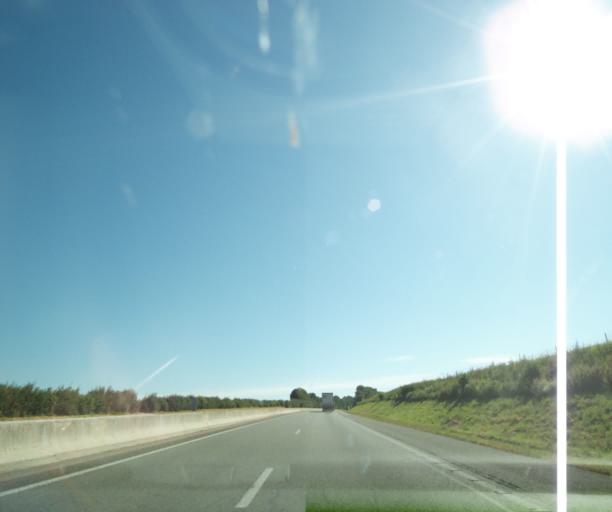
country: FR
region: Champagne-Ardenne
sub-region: Departement de la Haute-Marne
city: Avrecourt
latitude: 47.9626
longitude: 5.4674
